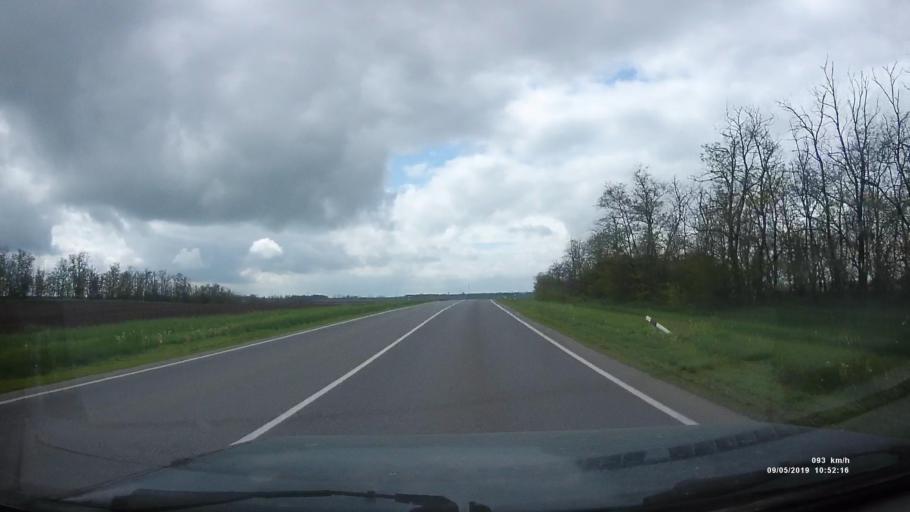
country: RU
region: Rostov
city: Peshkovo
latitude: 46.9026
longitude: 39.3536
